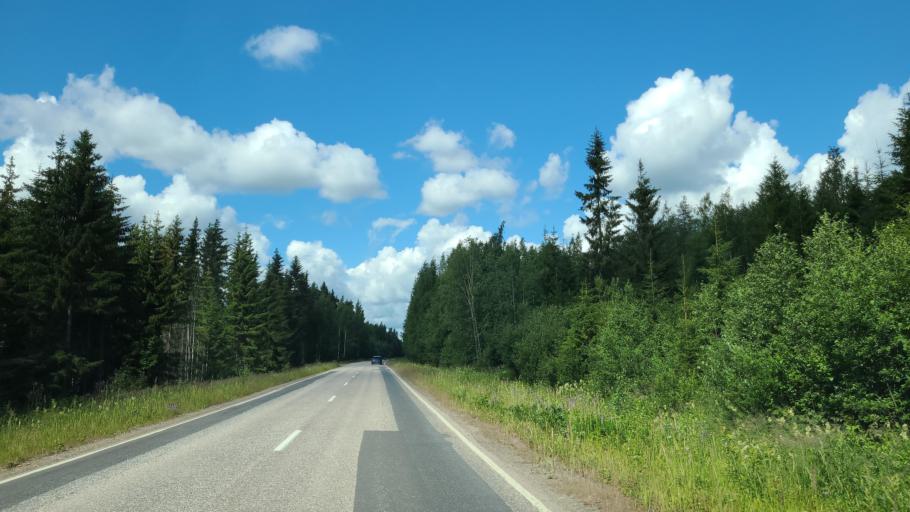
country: FI
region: Northern Savo
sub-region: Koillis-Savo
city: Kaavi
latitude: 62.9047
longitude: 28.7270
